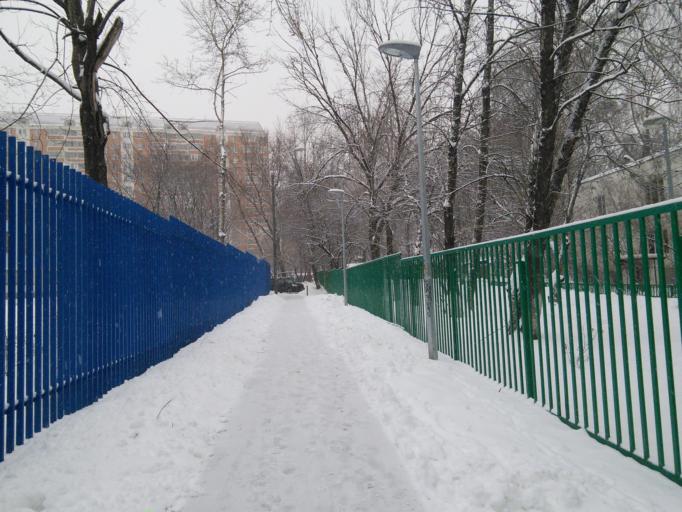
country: RU
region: Moscow
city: Leonovo
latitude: 55.8836
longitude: 37.6492
